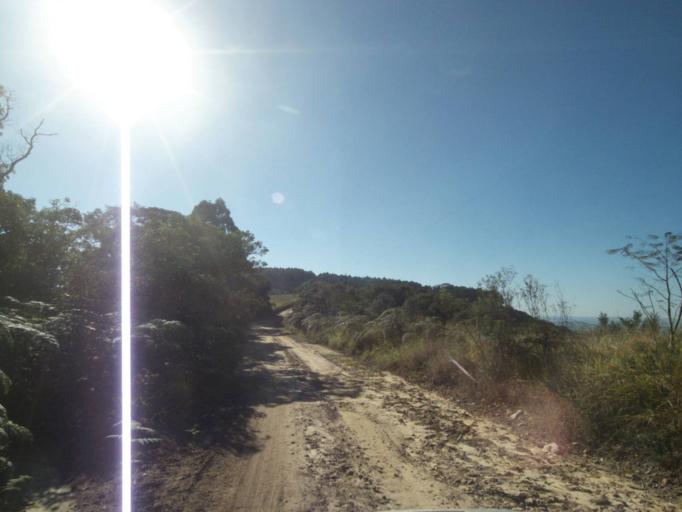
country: BR
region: Parana
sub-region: Tibagi
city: Tibagi
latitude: -24.5637
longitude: -50.4715
